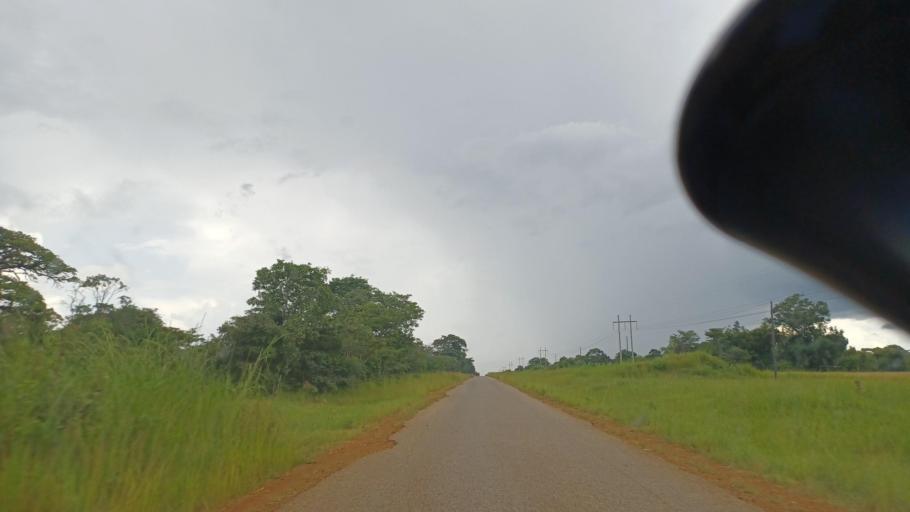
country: ZM
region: North-Western
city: Kasempa
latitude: -13.0218
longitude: 26.0001
